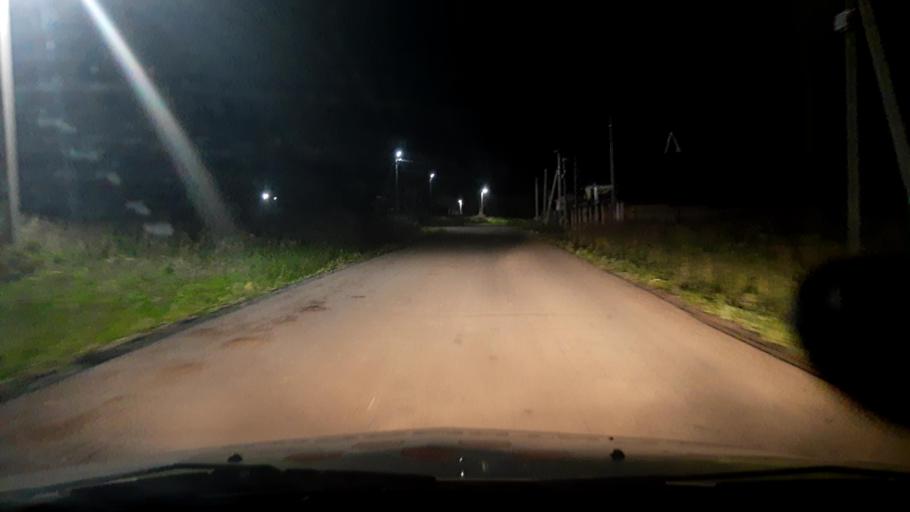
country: RU
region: Bashkortostan
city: Kabakovo
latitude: 54.5954
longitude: 56.2071
